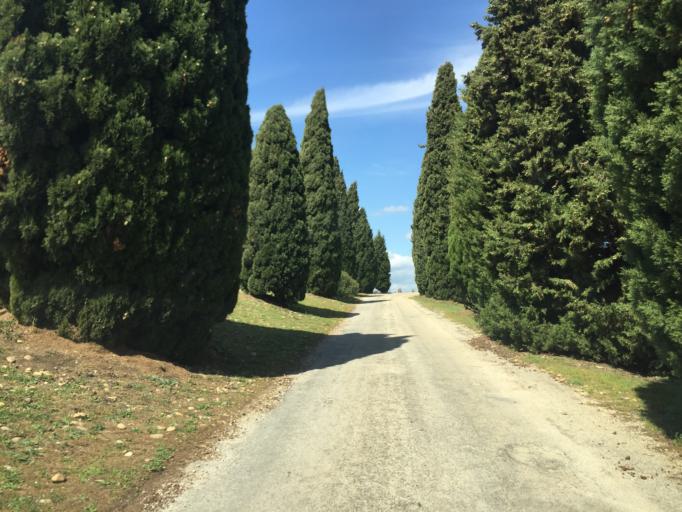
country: FR
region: Provence-Alpes-Cote d'Azur
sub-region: Departement du Vaucluse
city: Chateauneuf-du-Pape
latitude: 44.0494
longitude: 4.8479
